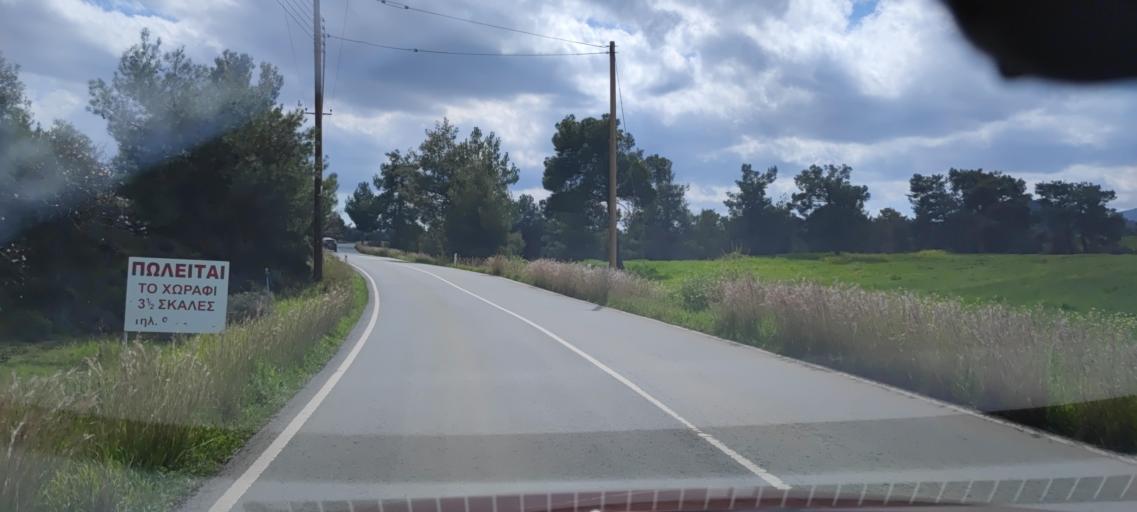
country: CY
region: Lefkosia
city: Lythrodontas
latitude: 34.9781
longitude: 33.2961
